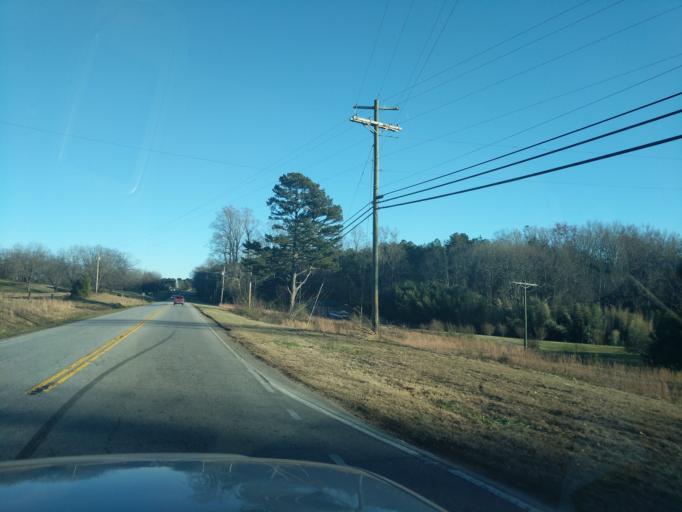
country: US
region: South Carolina
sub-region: Oconee County
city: Westminster
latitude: 34.6821
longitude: -83.1242
